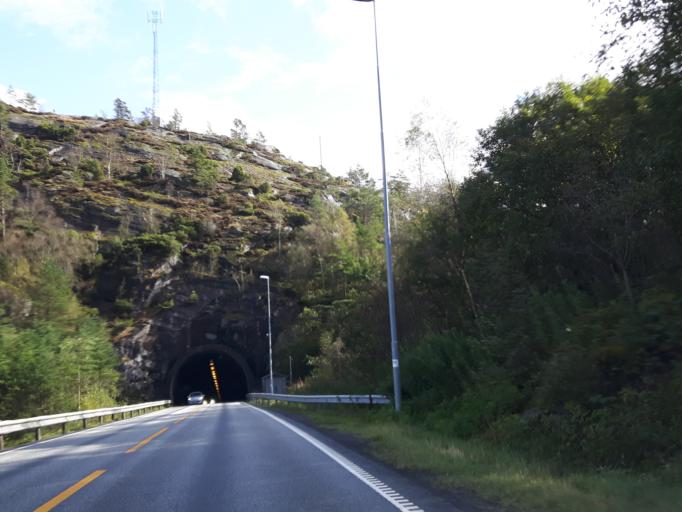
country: NO
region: Vest-Agder
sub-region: Flekkefjord
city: Flekkefjord
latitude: 58.2697
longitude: 6.7649
